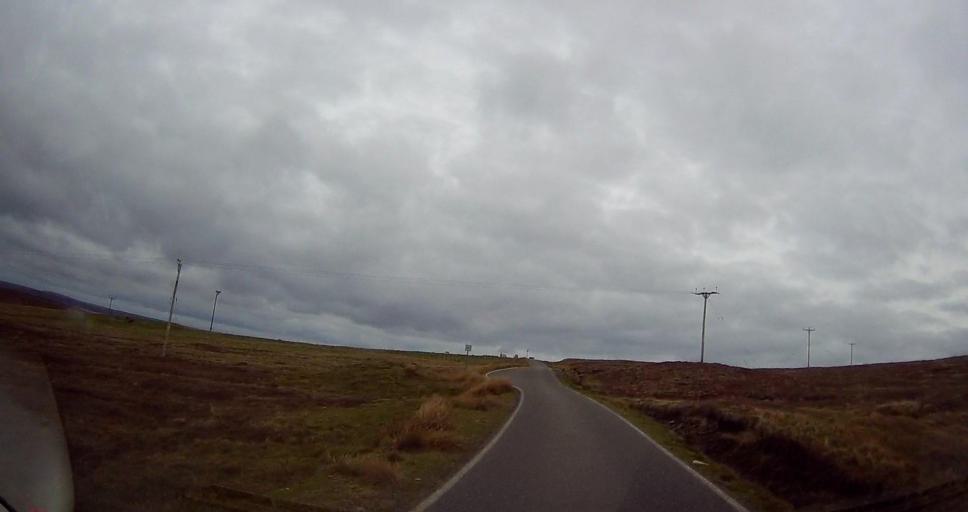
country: GB
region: Scotland
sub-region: Shetland Islands
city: Shetland
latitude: 60.5456
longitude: -1.0596
